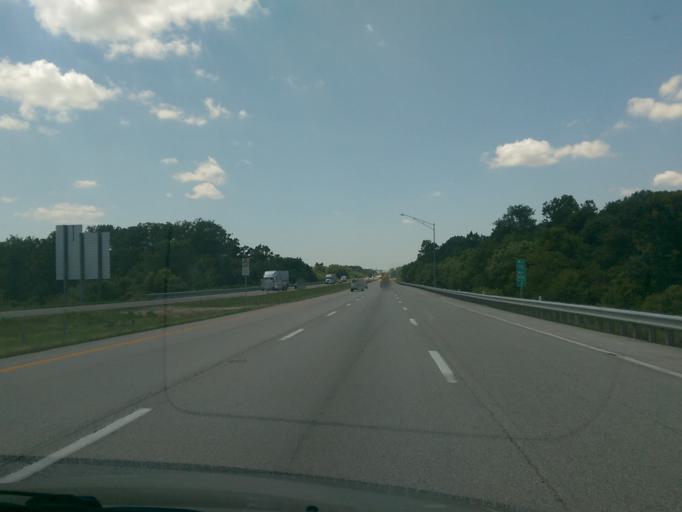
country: US
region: Missouri
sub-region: Cooper County
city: Boonville
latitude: 38.9377
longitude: -92.6951
